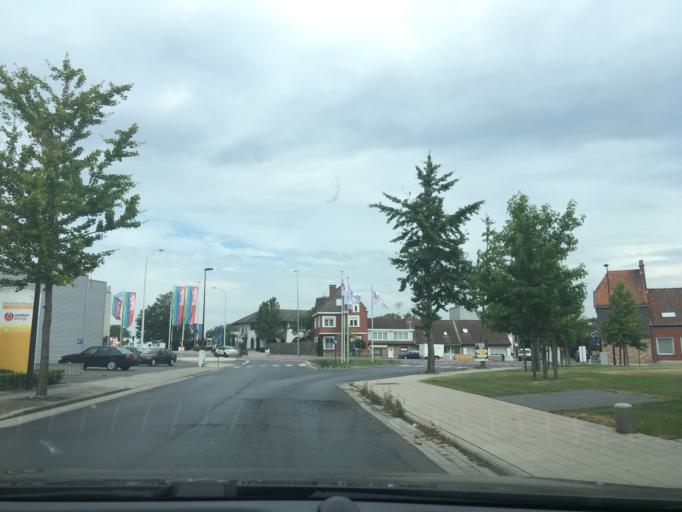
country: BE
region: Flanders
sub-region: Provincie West-Vlaanderen
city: Tielt
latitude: 50.9975
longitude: 3.3139
